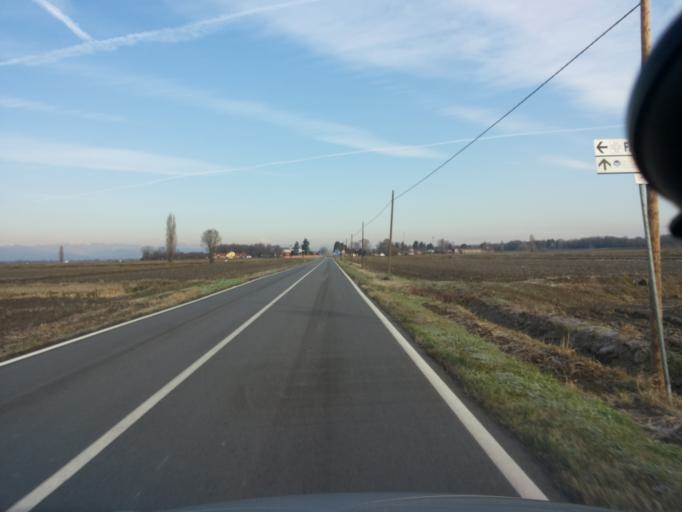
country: IT
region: Piedmont
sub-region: Provincia di Vercelli
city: Albano Vercellese
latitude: 45.4161
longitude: 8.3790
